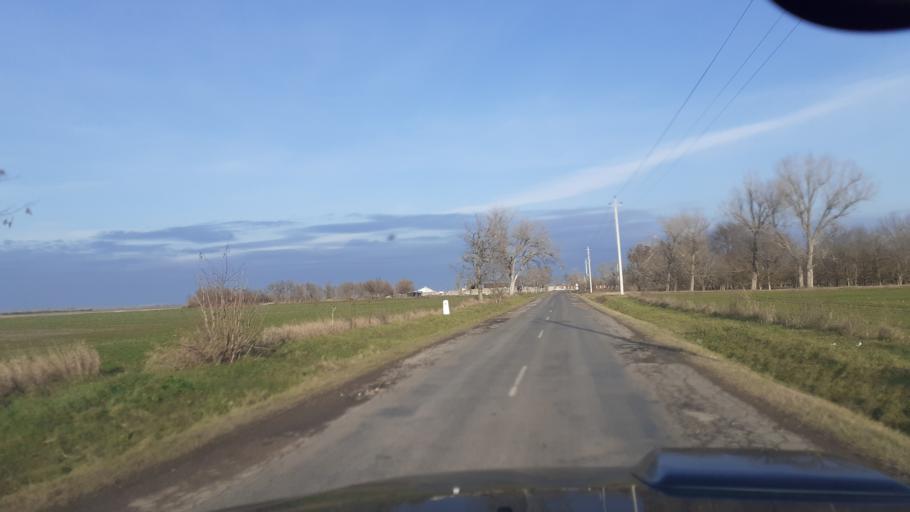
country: HU
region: Pest
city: Domsod
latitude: 47.1068
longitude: 19.0531
